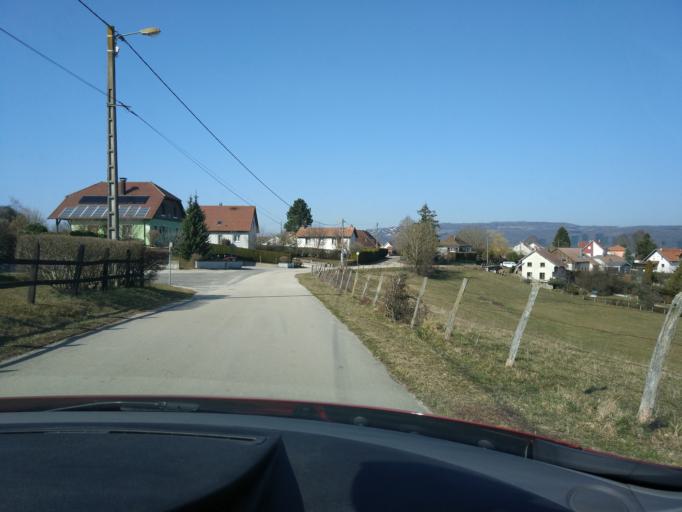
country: FR
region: Franche-Comte
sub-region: Departement du Doubs
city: Saone
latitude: 47.2189
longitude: 6.1205
